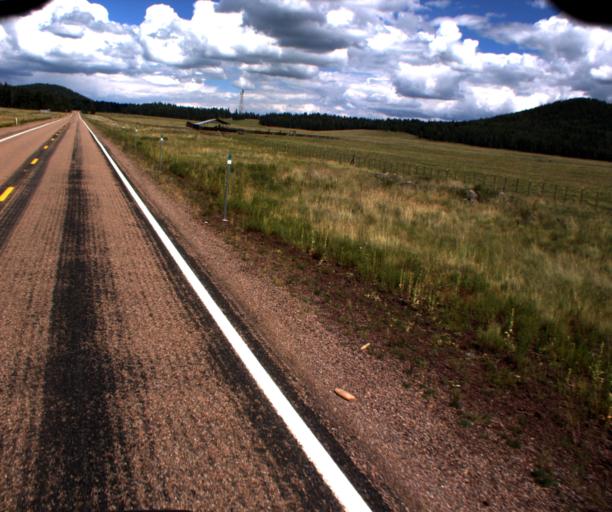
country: US
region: Arizona
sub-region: Apache County
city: Eagar
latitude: 34.0459
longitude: -109.5870
